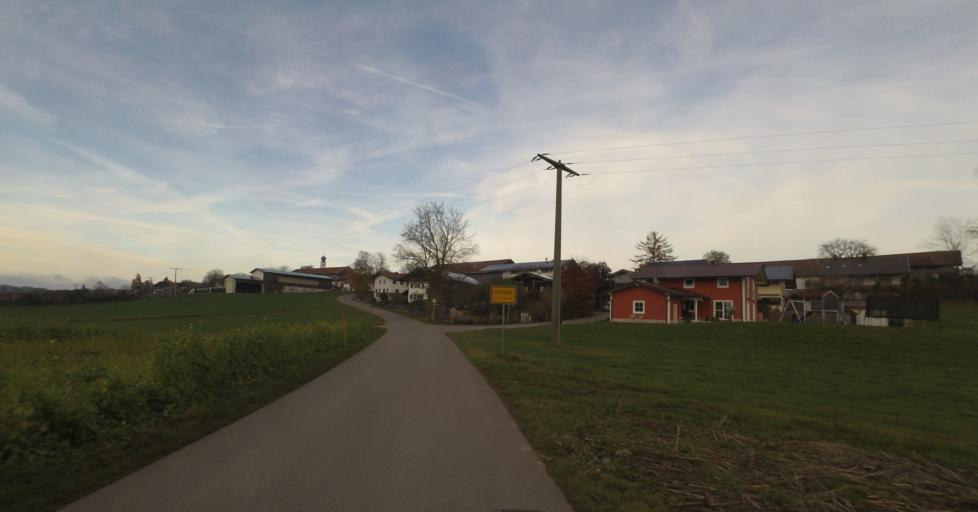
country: DE
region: Bavaria
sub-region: Upper Bavaria
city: Nussdorf
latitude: 47.9023
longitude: 12.5952
